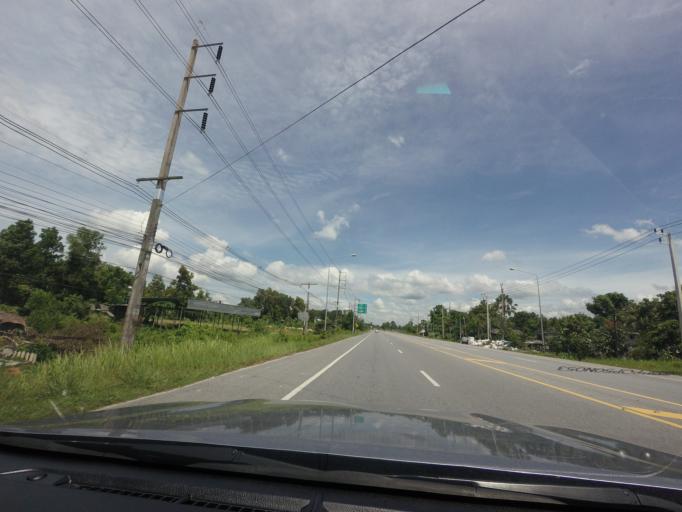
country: TH
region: Songkhla
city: Chana
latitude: 6.9854
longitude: 100.6795
